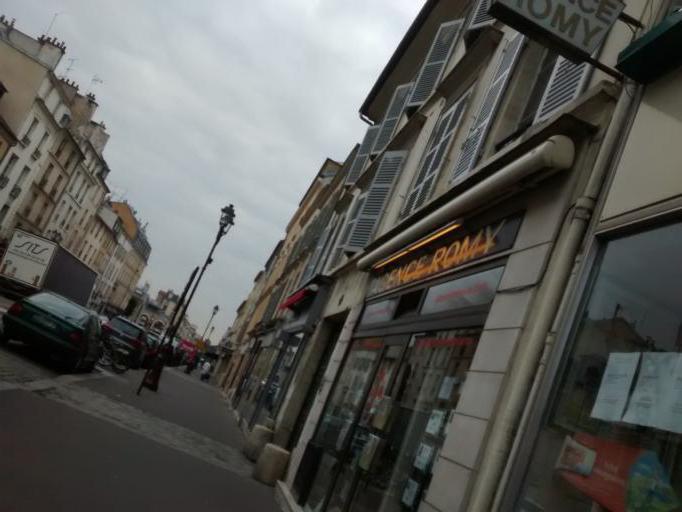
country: FR
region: Ile-de-France
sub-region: Departement des Yvelines
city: Versailles
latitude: 48.8060
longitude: 2.1344
